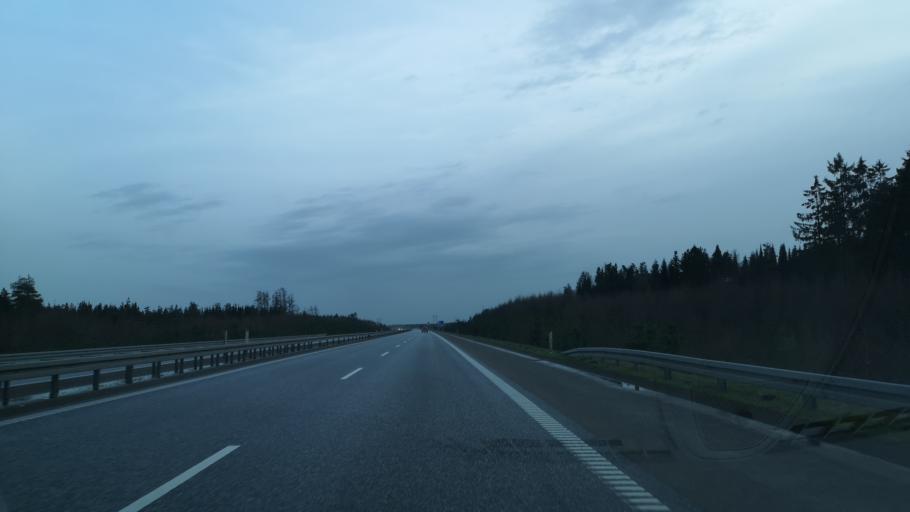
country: DK
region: Central Jutland
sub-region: Herning Kommune
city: Lind
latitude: 56.0520
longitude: 8.9994
